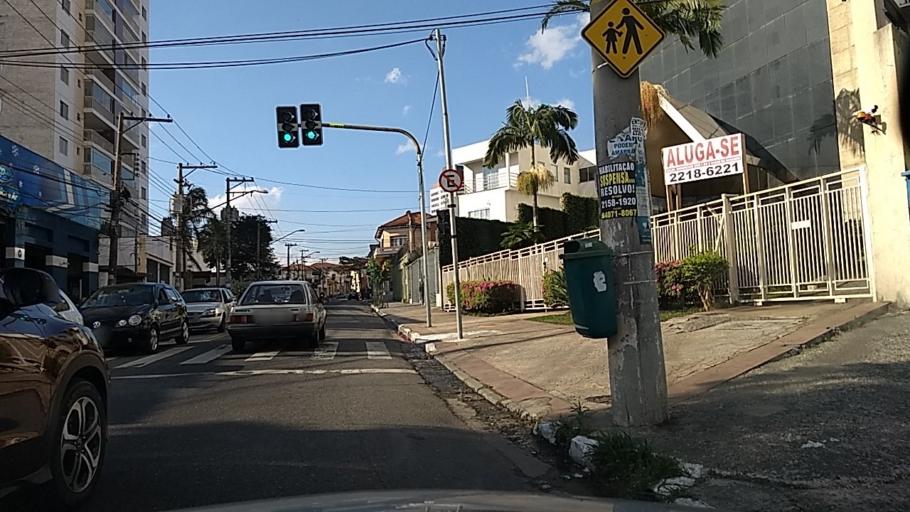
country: BR
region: Sao Paulo
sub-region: Sao Paulo
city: Sao Paulo
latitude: -23.5016
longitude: -46.6120
